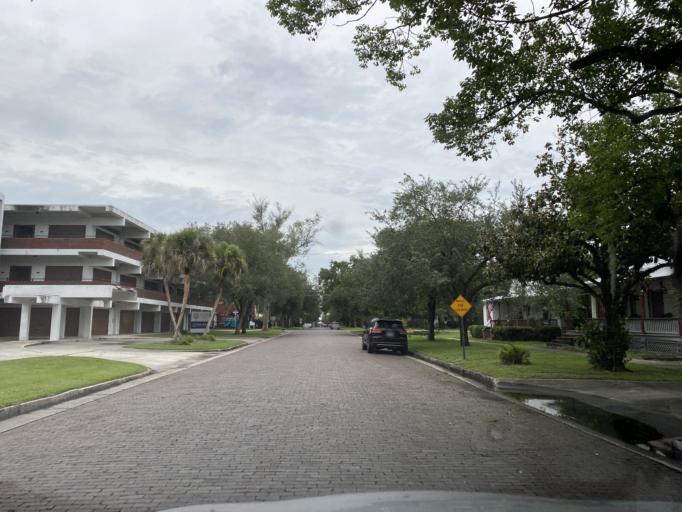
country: US
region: Florida
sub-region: Seminole County
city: Sanford
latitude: 28.8072
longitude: -81.2669
